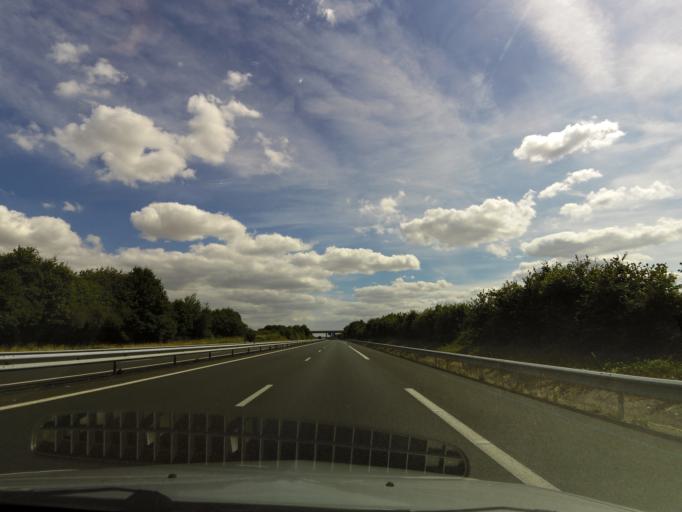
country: FR
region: Pays de la Loire
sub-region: Departement de la Vendee
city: Les Essarts
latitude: 46.8190
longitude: -1.2167
